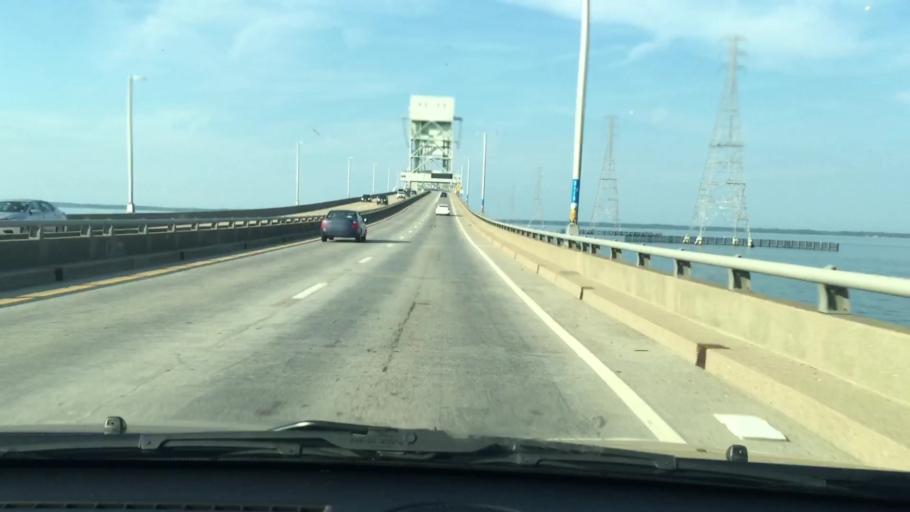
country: US
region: Virginia
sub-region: City of Newport News
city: Newport News
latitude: 37.0063
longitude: -76.4646
